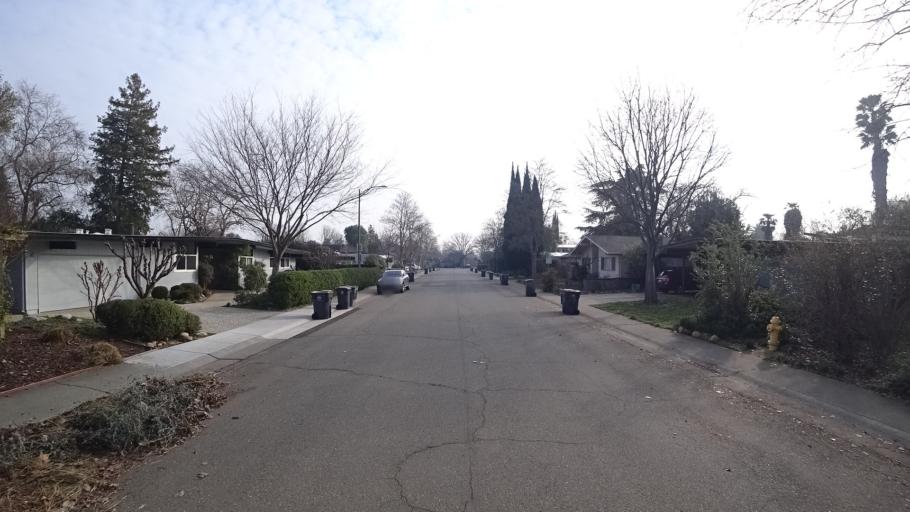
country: US
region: California
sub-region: Yolo County
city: Davis
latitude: 38.5548
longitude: -121.7639
